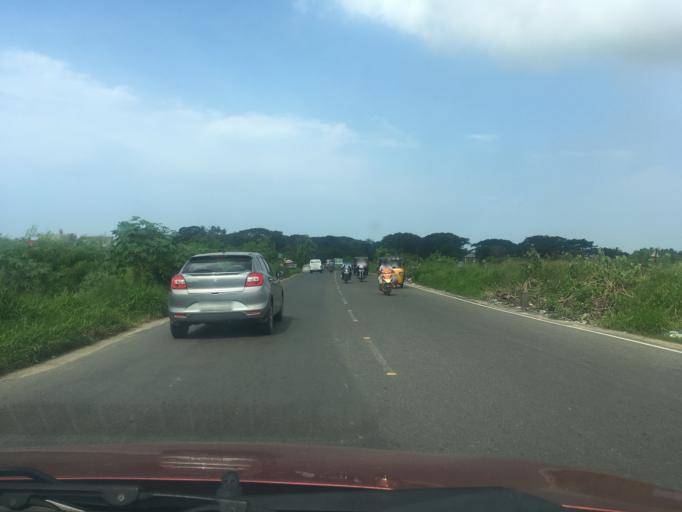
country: IN
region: Kerala
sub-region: Ernakulam
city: Cochin
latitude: 9.9367
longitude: 76.2749
